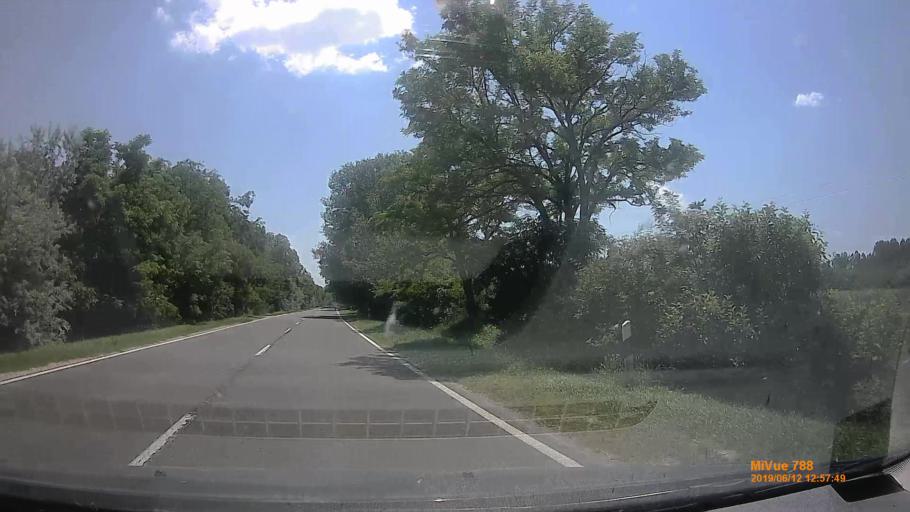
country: HU
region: Bacs-Kiskun
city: Palmonostora
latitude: 46.6304
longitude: 19.8953
